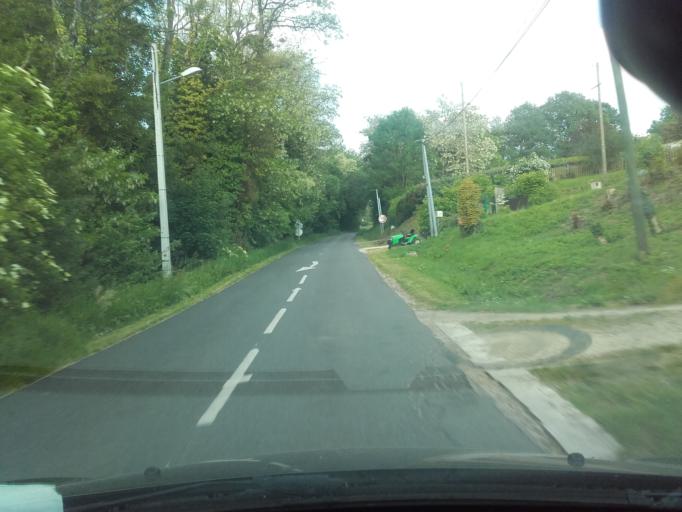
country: FR
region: Centre
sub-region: Departement du Loir-et-Cher
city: Chouzy-sur-Cisse
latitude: 47.5421
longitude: 1.2347
